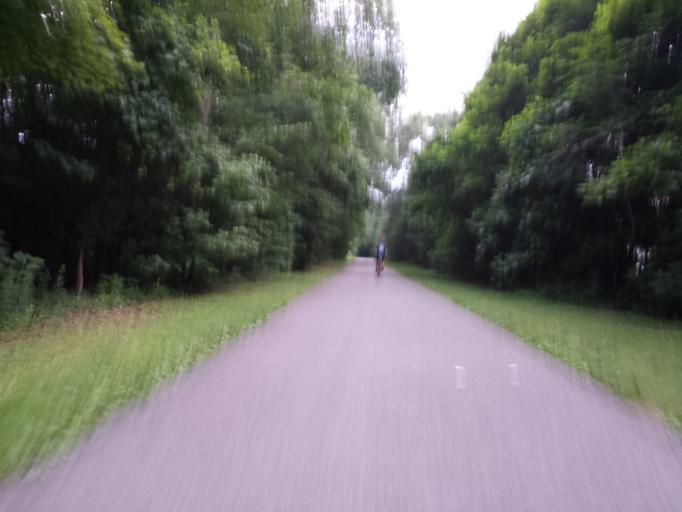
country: US
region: New York
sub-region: Ulster County
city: Highland
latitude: 41.7309
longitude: -73.9720
